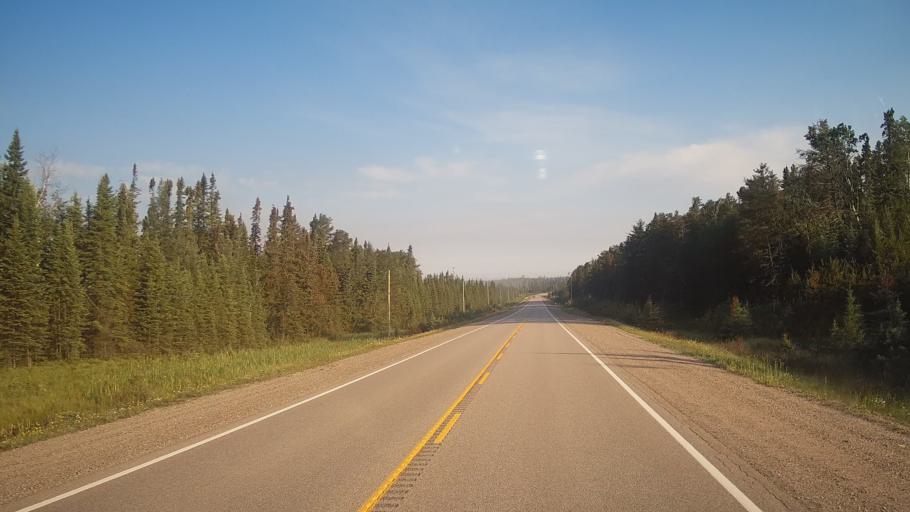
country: CA
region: Ontario
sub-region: Rainy River District
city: Atikokan
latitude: 49.3829
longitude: -91.5898
